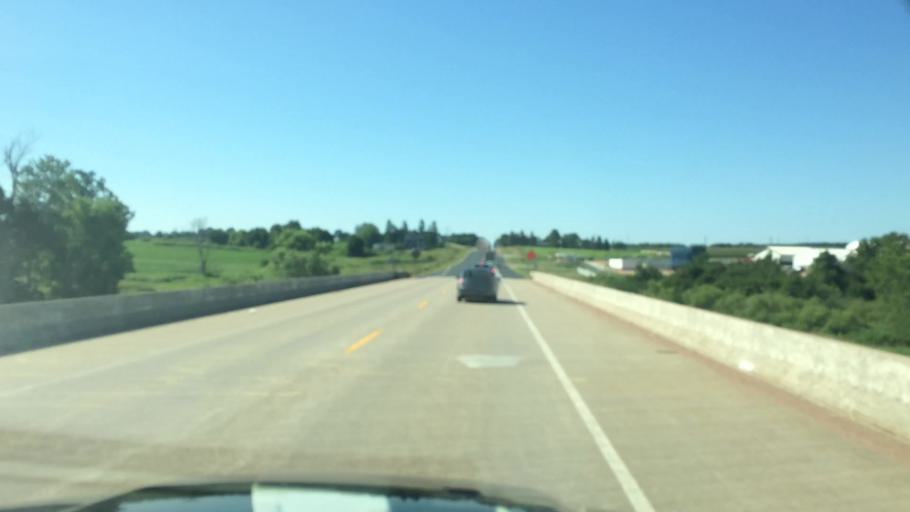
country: US
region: Wisconsin
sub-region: Marathon County
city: Stratford
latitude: 44.8218
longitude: -90.0791
